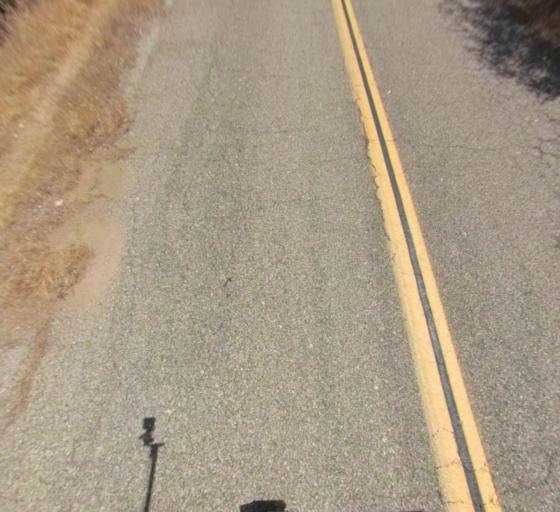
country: US
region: California
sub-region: Fresno County
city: Auberry
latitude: 37.1554
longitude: -119.5130
